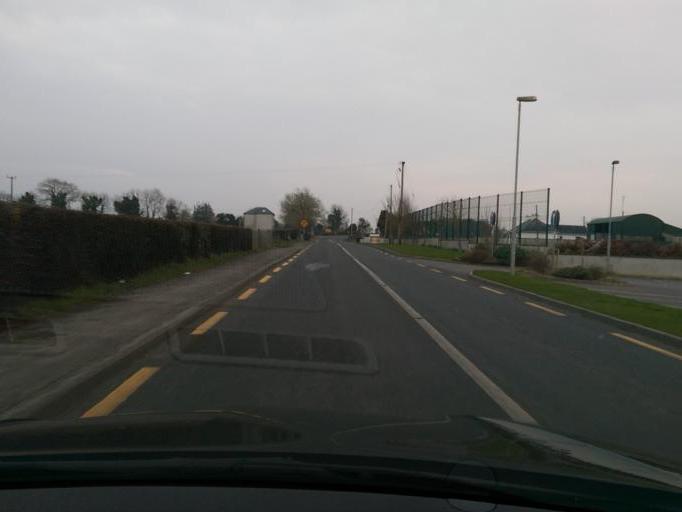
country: IE
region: Leinster
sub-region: An Longfort
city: Ballymahon
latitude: 53.5344
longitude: -7.7924
